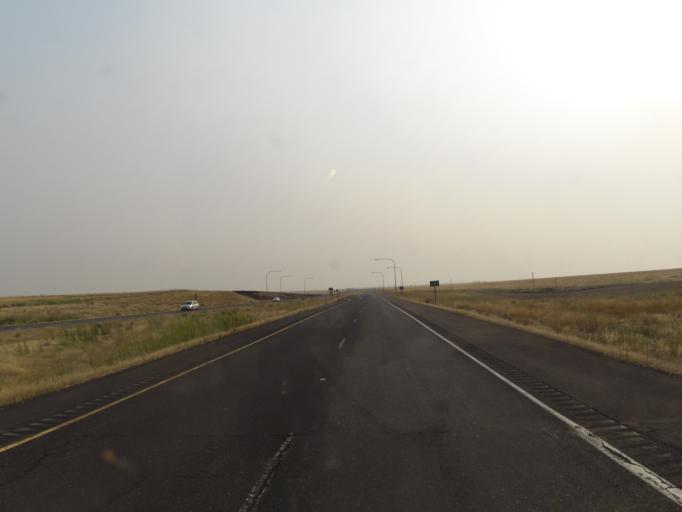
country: US
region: Washington
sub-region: Franklin County
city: Connell
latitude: 46.7359
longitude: -118.8192
